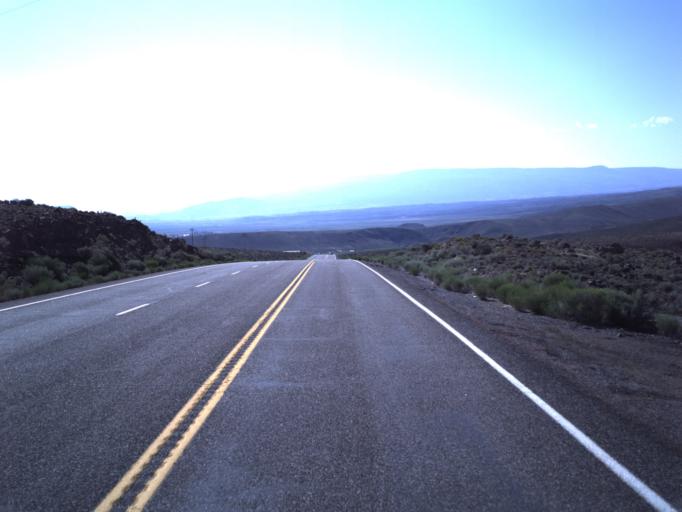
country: US
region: Utah
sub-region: Wayne County
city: Loa
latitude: 38.4327
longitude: -111.6962
